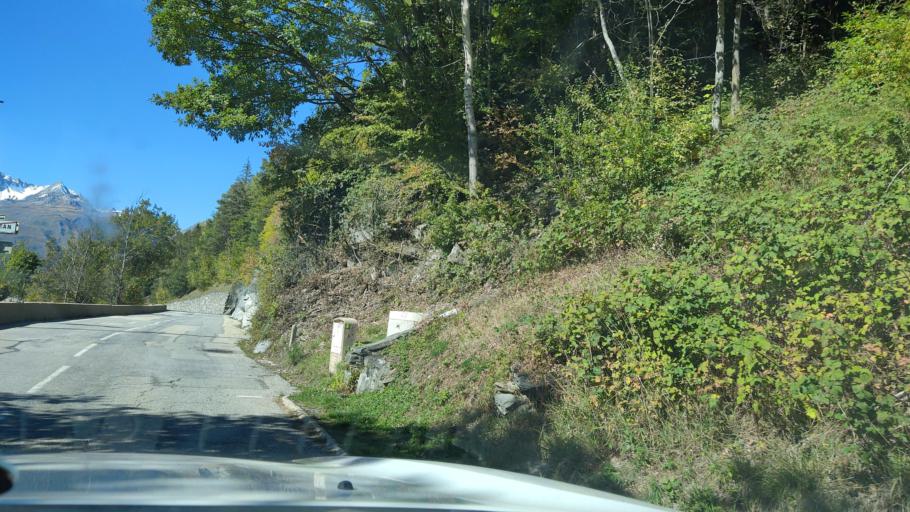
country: FR
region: Rhone-Alpes
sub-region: Departement de la Savoie
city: Seez
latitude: 45.6123
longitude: 6.8444
